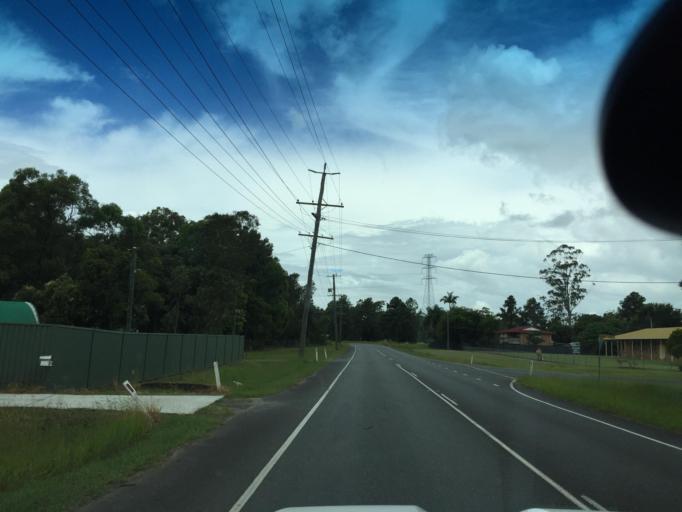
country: AU
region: Queensland
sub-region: Moreton Bay
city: Caboolture
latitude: -27.0670
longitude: 152.9140
